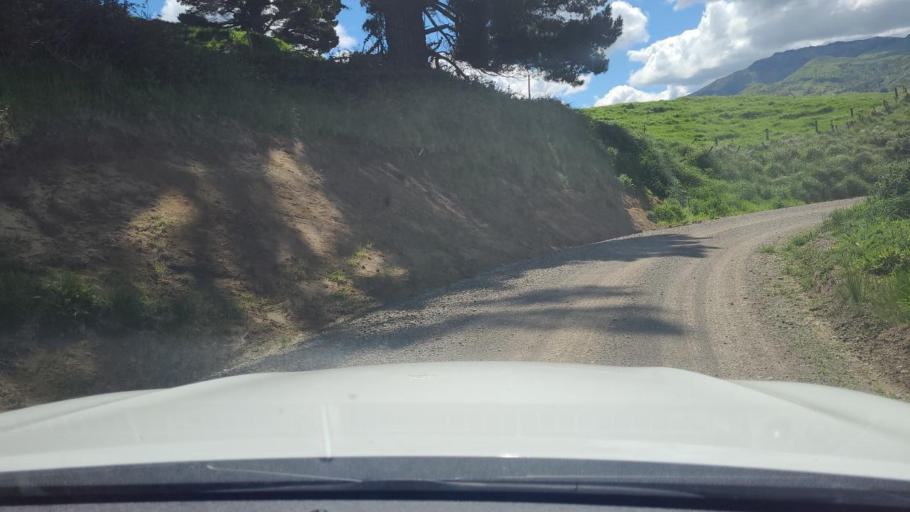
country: NZ
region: Hawke's Bay
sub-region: Napier City
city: Napier
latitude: -39.1627
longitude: 176.6701
